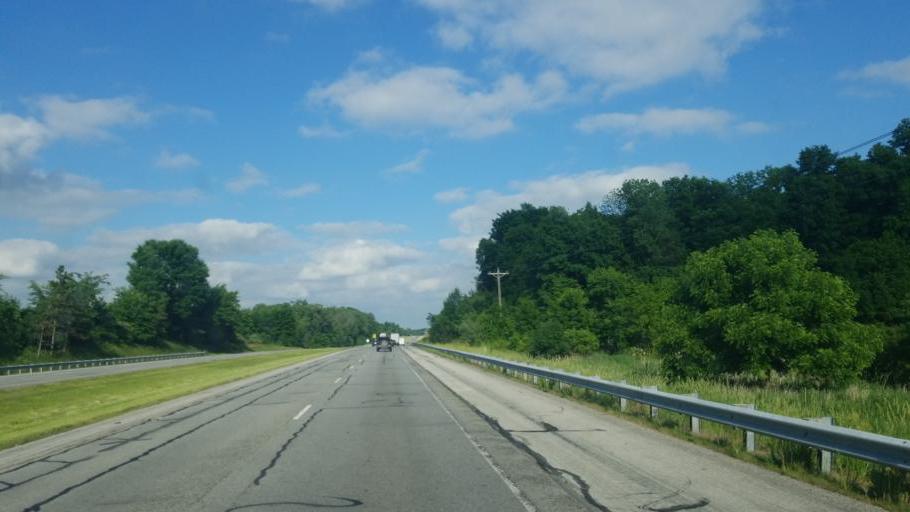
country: US
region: Indiana
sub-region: Whitley County
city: Columbia City
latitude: 41.1775
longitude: -85.5811
